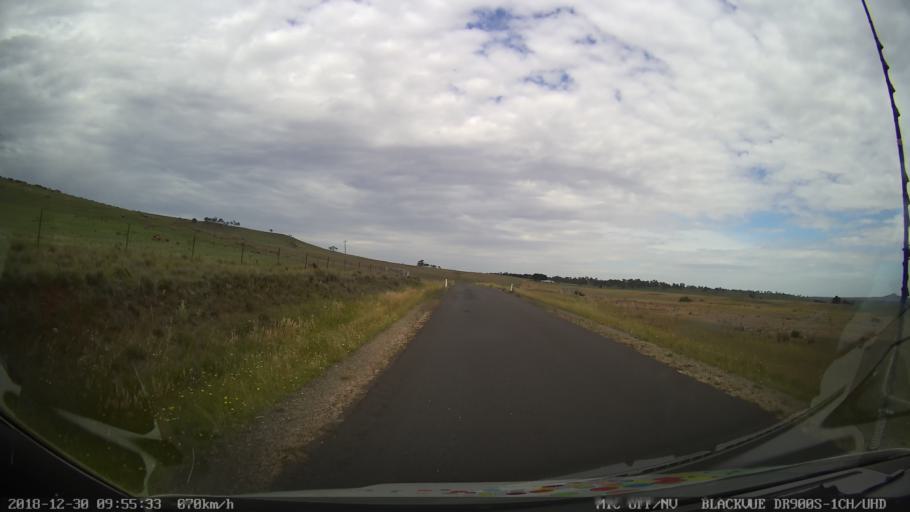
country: AU
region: New South Wales
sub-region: Cooma-Monaro
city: Cooma
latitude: -36.5212
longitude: 149.2631
